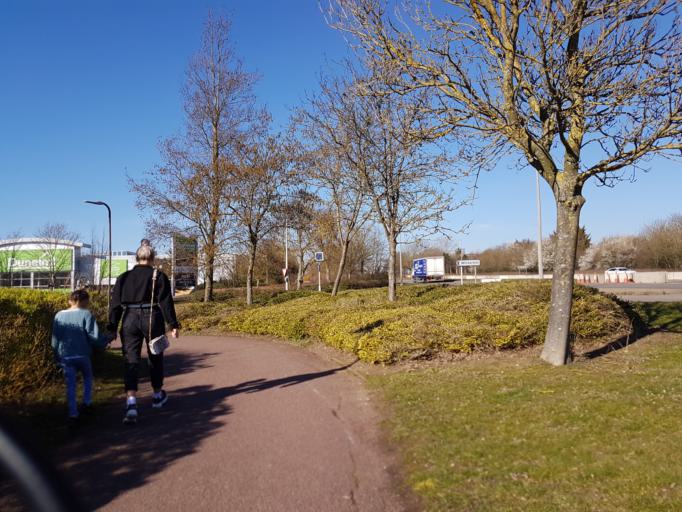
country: GB
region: England
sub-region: Milton Keynes
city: Milton Keynes
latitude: 52.0298
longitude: -0.7639
